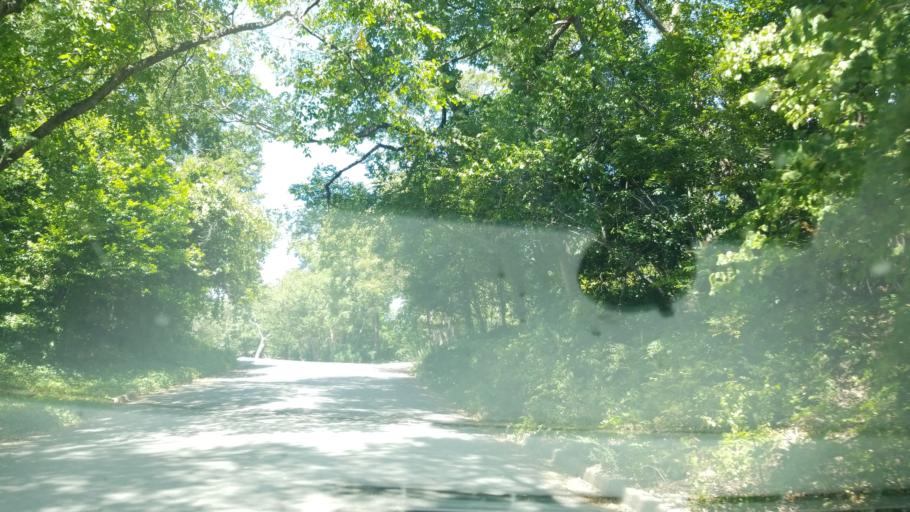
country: US
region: Texas
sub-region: Dallas County
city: Dallas
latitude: 32.7619
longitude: -96.8311
